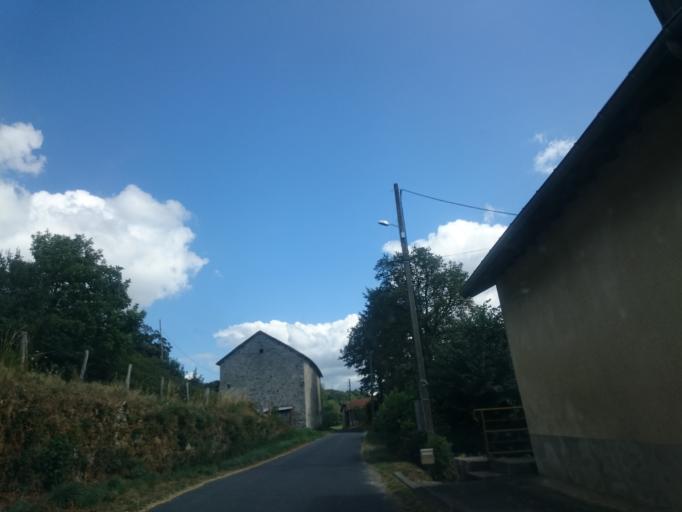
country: FR
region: Auvergne
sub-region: Departement du Cantal
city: Laroquebrou
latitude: 44.8965
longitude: 2.2039
